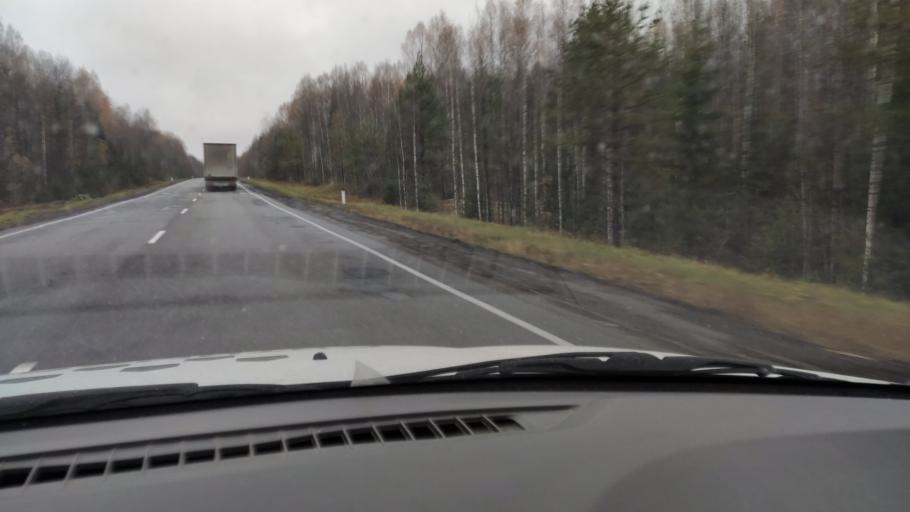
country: RU
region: Kirov
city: Omutninsk
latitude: 58.7653
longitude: 51.9852
